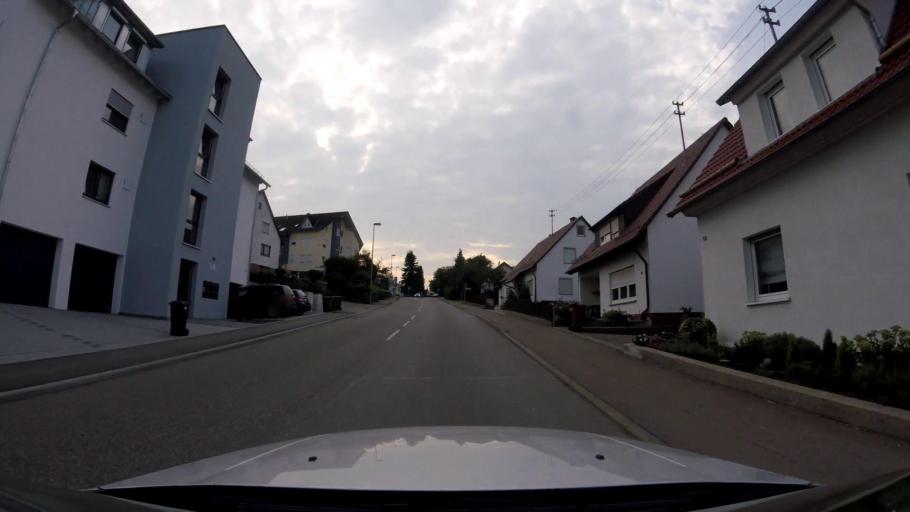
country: DE
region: Baden-Wuerttemberg
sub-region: Regierungsbezirk Stuttgart
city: Rudersberg
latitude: 48.8859
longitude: 9.5236
